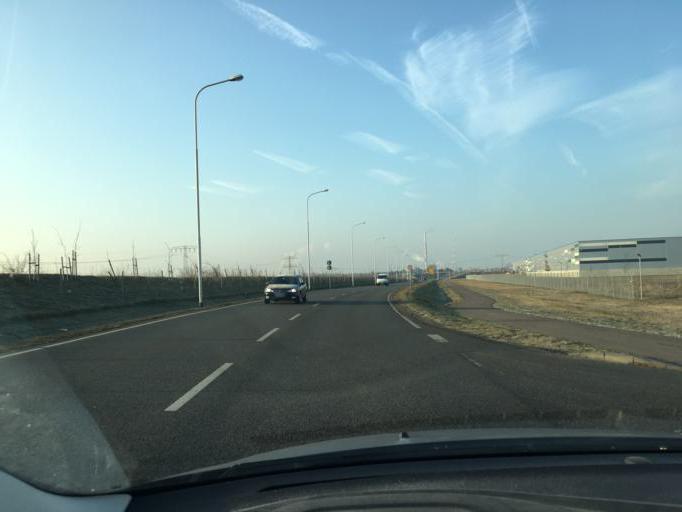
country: DE
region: Saxony-Anhalt
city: Halle (Saale)
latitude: 51.4751
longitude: 12.0162
